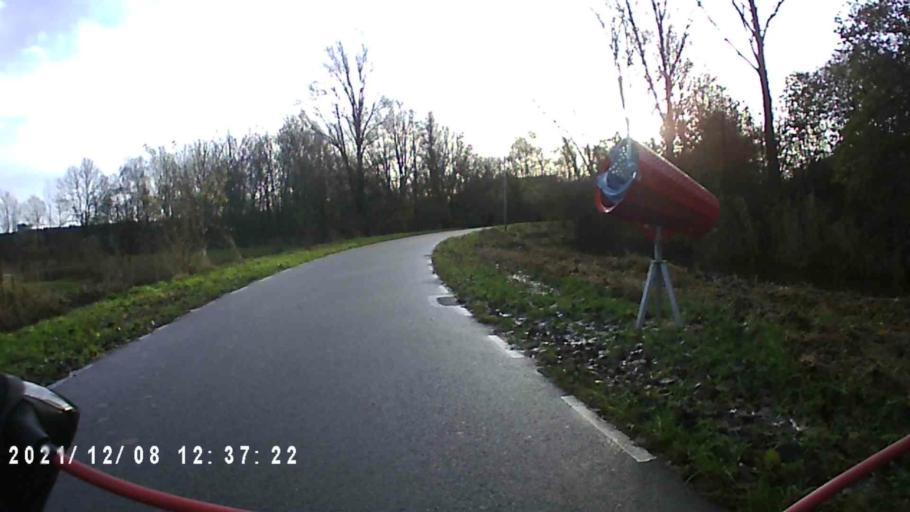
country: NL
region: Groningen
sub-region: Gemeente Groningen
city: Oosterpark
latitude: 53.2115
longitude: 6.6095
